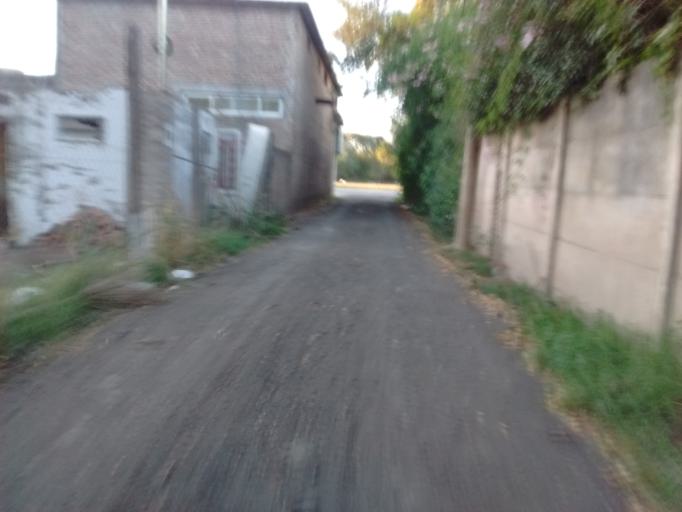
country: AR
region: Santa Fe
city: Funes
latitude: -32.9188
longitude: -60.8301
